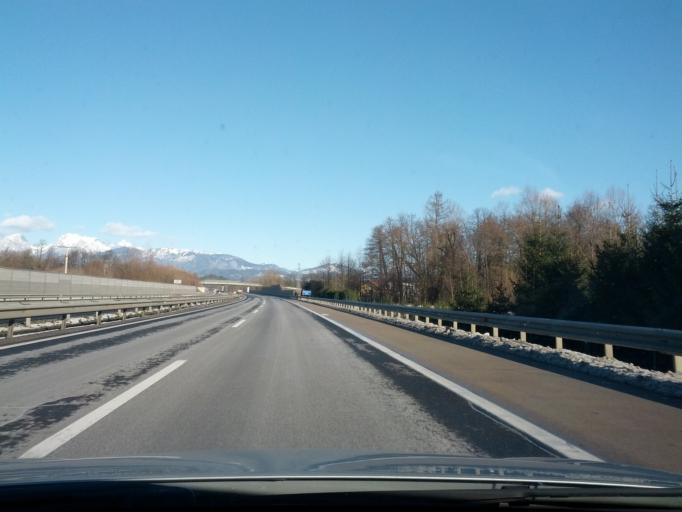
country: SI
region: Dol pri Ljubljani
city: Dol pri Ljubljani
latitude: 46.1090
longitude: 14.6002
